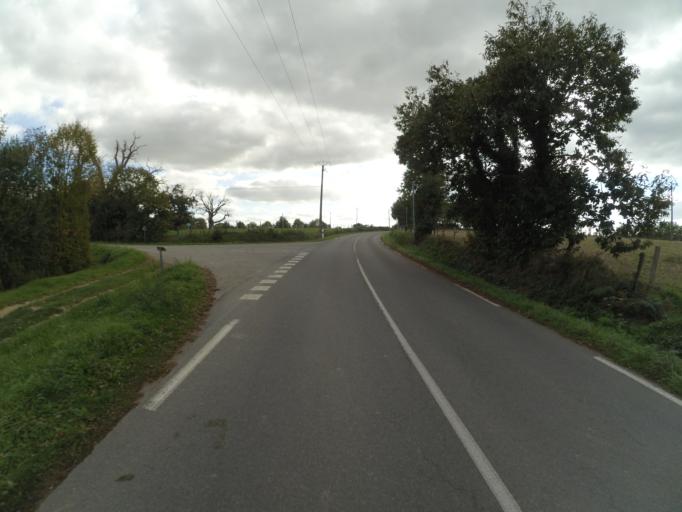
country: FR
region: Pays de la Loire
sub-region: Departement de la Loire-Atlantique
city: Suce-sur-Erdre
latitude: 47.3204
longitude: -1.5106
